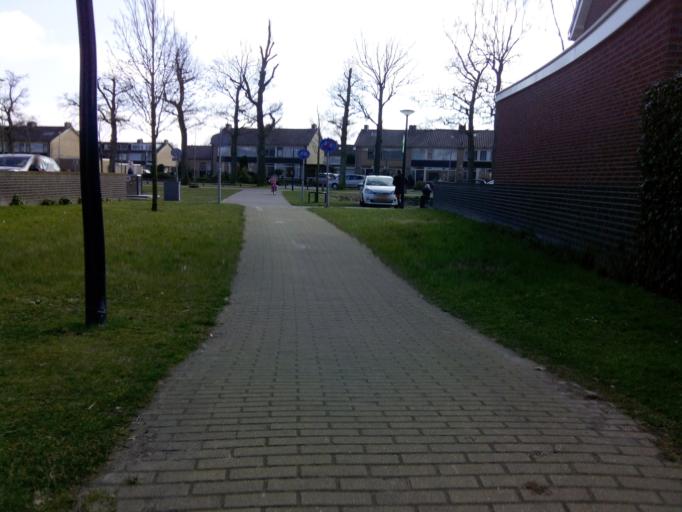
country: NL
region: Utrecht
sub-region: Gemeente Utrechtse Heuvelrug
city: Overberg
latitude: 52.0849
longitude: 5.4798
